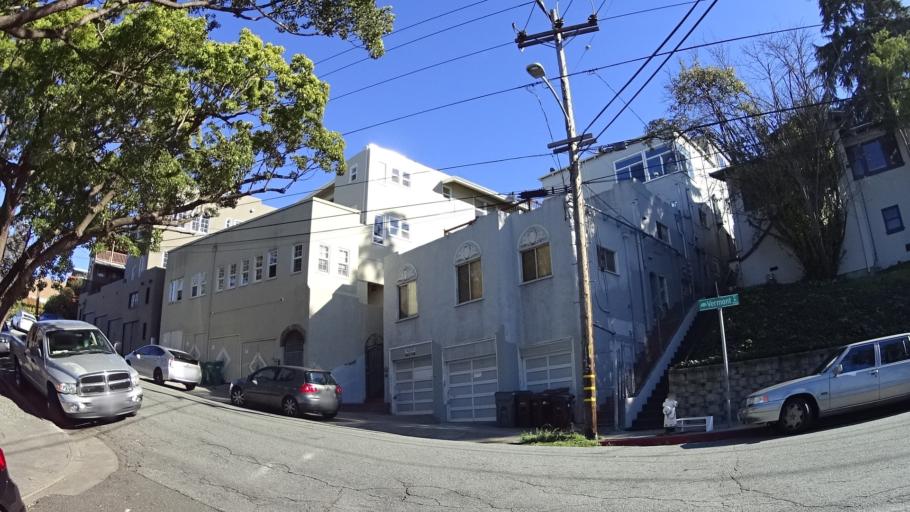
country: US
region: California
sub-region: Alameda County
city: Piedmont
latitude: 37.8161
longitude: -122.2432
